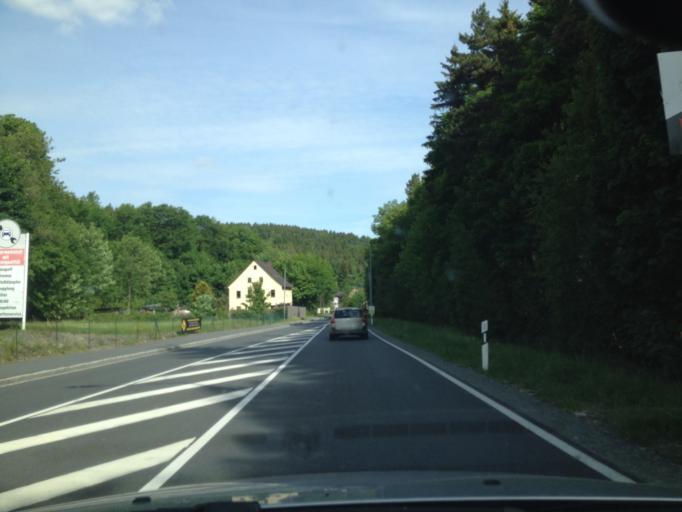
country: DE
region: Saxony
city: Ehrenfriedersdorf
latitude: 50.6584
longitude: 12.9689
